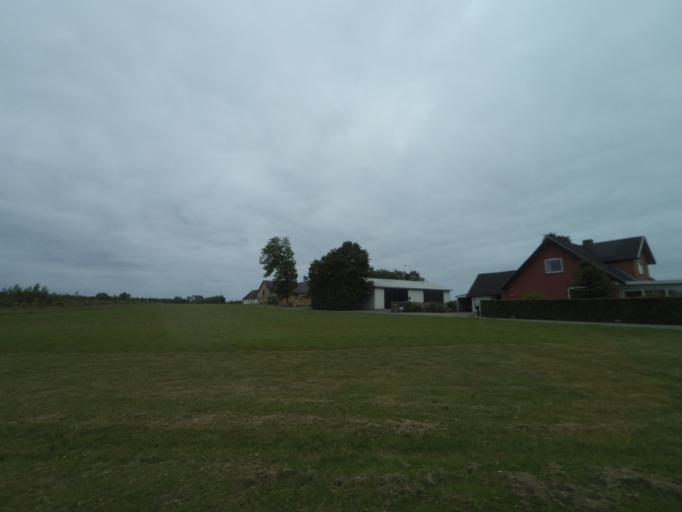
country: DK
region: South Denmark
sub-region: Nordfyns Kommune
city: Otterup
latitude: 55.5579
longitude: 10.4314
